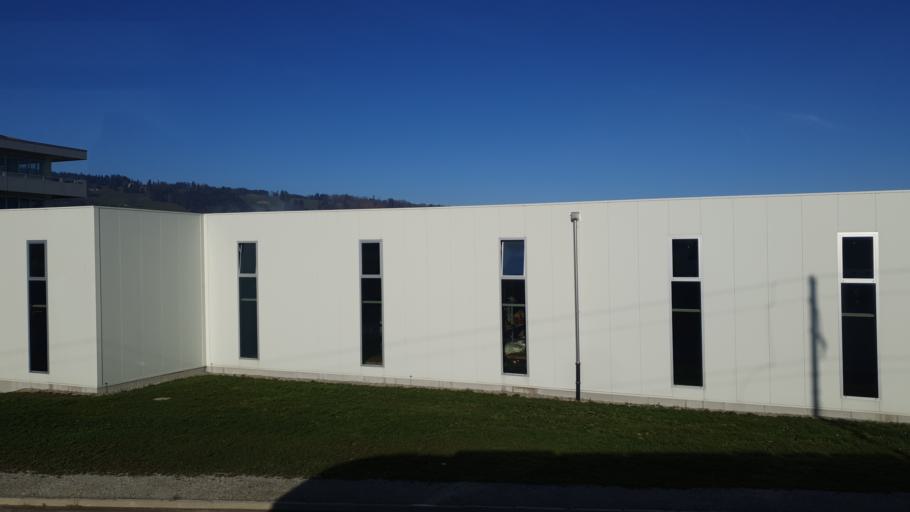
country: CH
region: Fribourg
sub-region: Gruyere District
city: Vuadens
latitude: 46.6215
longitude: 7.0367
